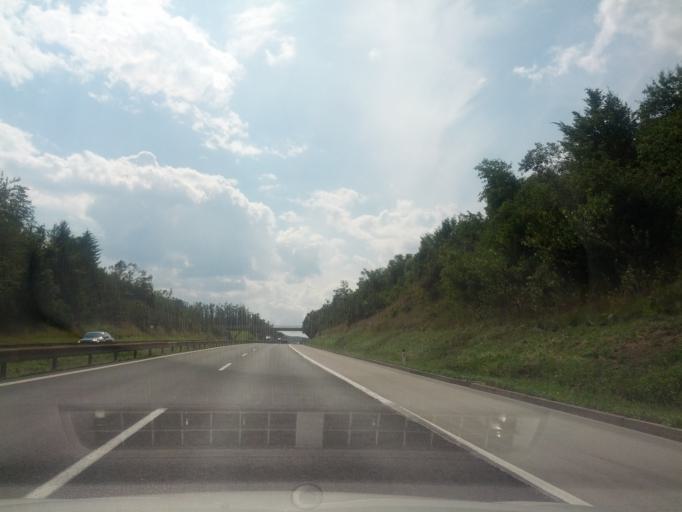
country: SI
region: Postojna
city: Postojna
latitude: 45.7597
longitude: 14.0923
